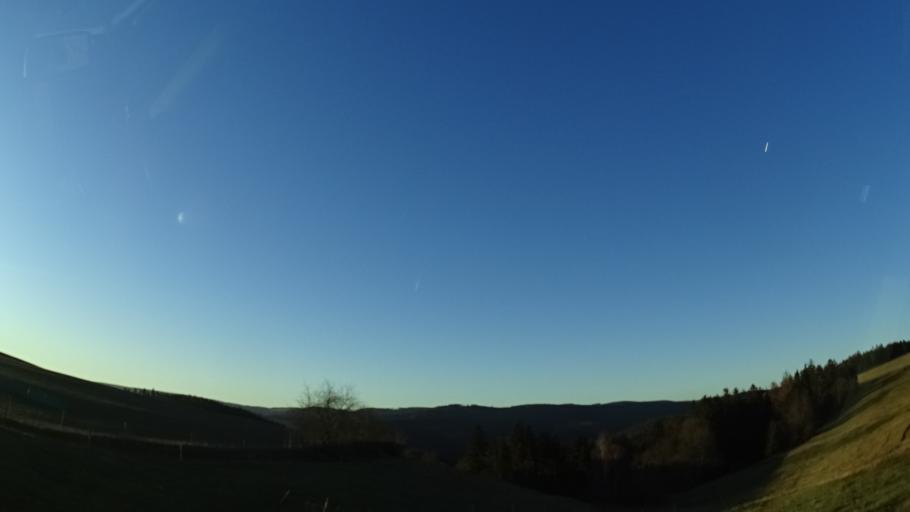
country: DE
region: Thuringia
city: Grafenthal
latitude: 50.5429
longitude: 11.2852
